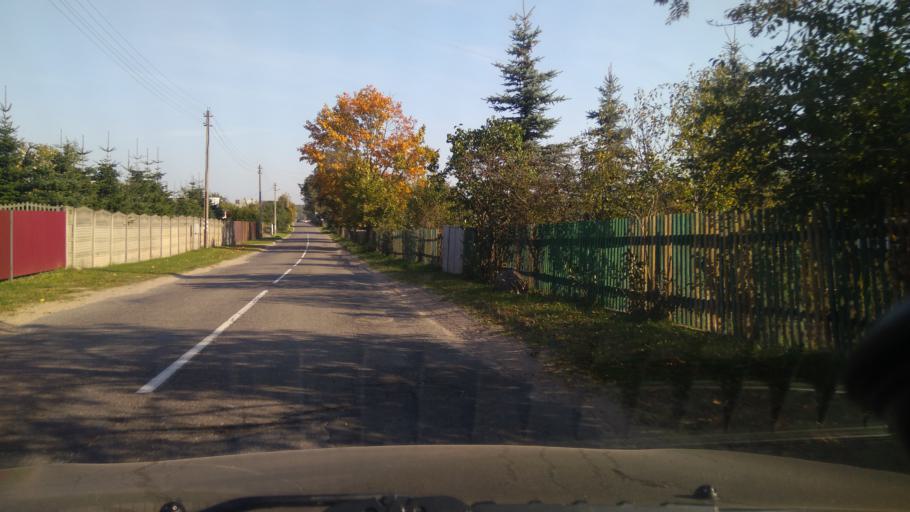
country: BY
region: Minsk
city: Rakaw
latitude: 54.0040
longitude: 27.0465
